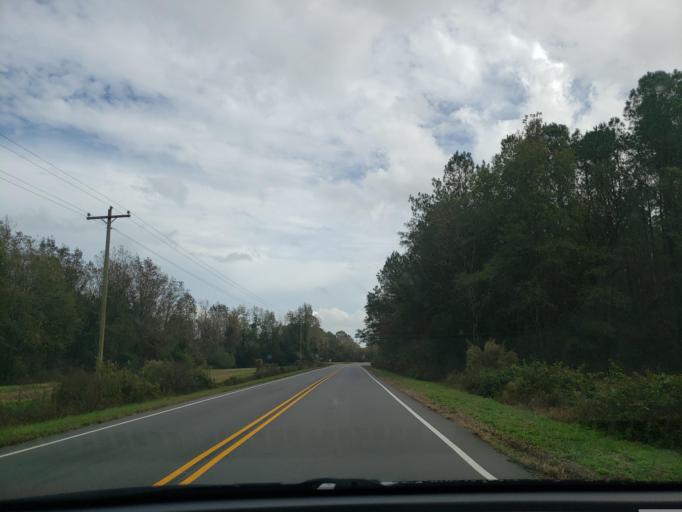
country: US
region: North Carolina
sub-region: Duplin County
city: Beulaville
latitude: 34.8308
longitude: -77.8503
